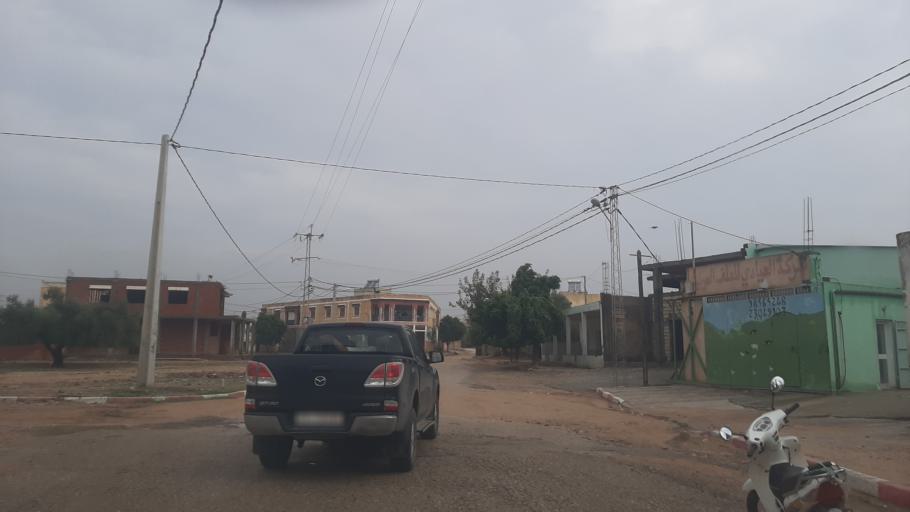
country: TN
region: Al Munastir
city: Sidi Bin Nur
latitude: 35.4810
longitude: 10.8731
